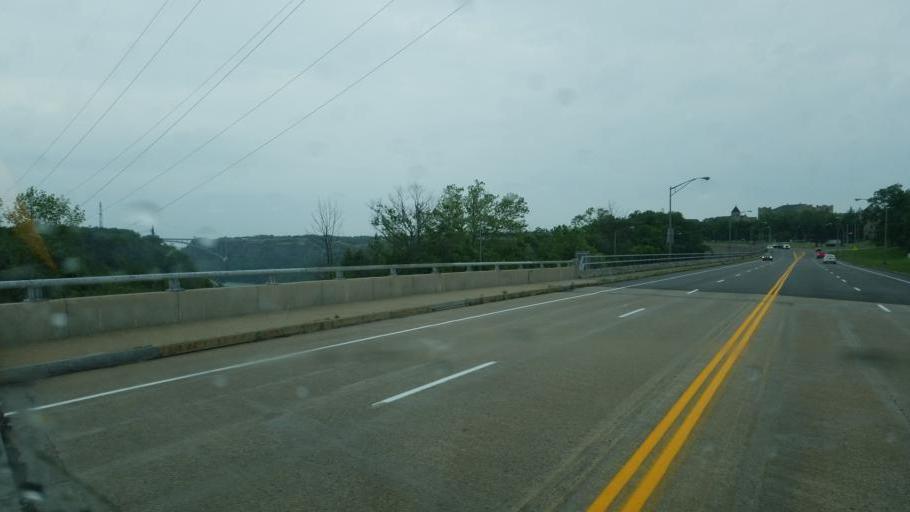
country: US
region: New York
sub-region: Niagara County
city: Lewiston
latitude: 43.1337
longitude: -79.0447
